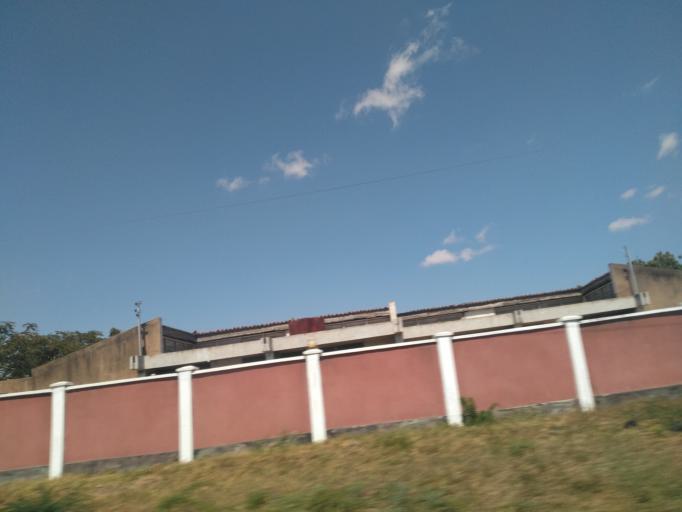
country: TZ
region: Dodoma
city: Dodoma
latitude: -6.1666
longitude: 35.7550
